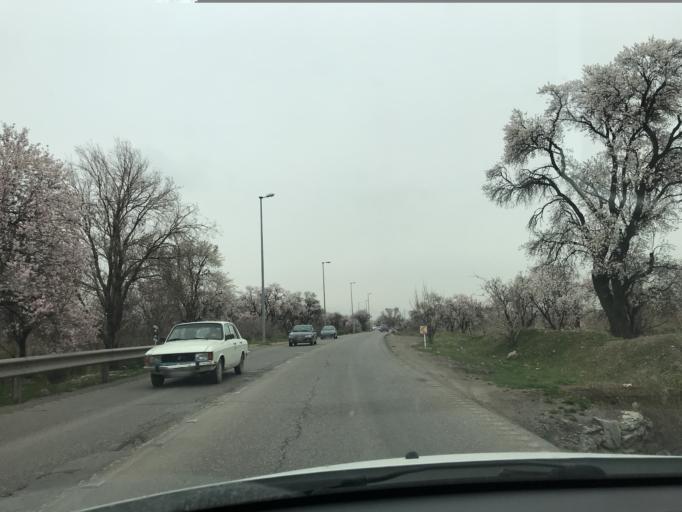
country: IR
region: Qazvin
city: Qazvin
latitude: 36.2787
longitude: 49.9812
